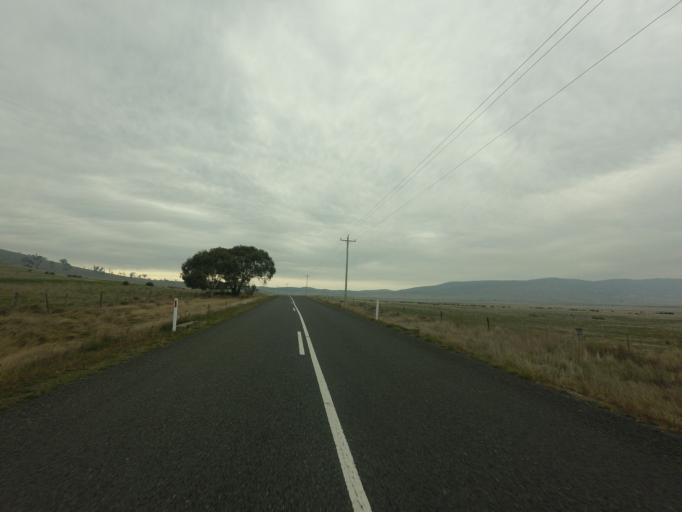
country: AU
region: Tasmania
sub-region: Derwent Valley
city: New Norfolk
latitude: -42.4430
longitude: 146.9752
